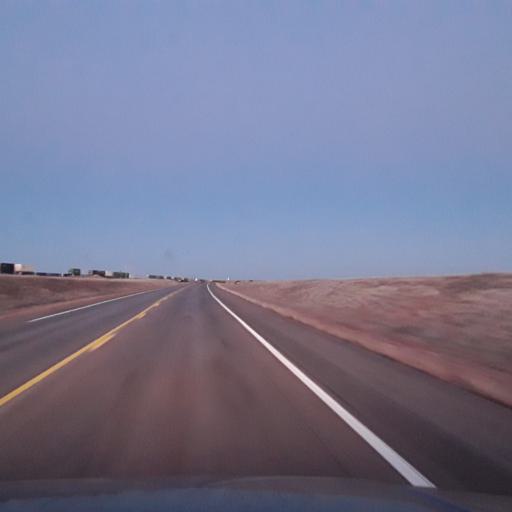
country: US
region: New Mexico
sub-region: Guadalupe County
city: Santa Rosa
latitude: 34.7493
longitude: -105.0123
